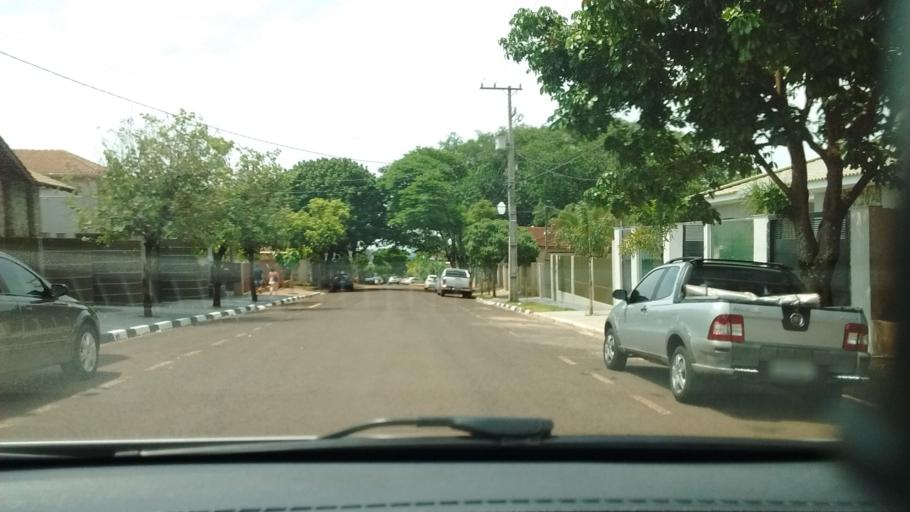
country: BR
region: Parana
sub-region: Corbelia
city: Corbelia
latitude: -24.5409
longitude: -52.9913
